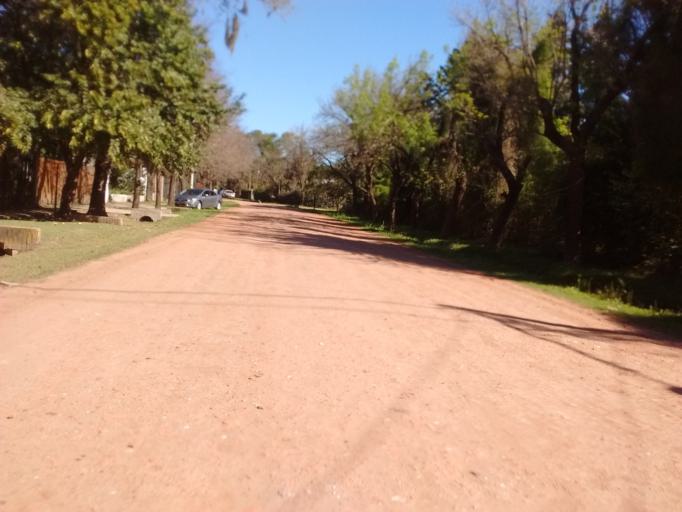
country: AR
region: Santa Fe
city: Funes
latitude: -32.9228
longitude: -60.8139
